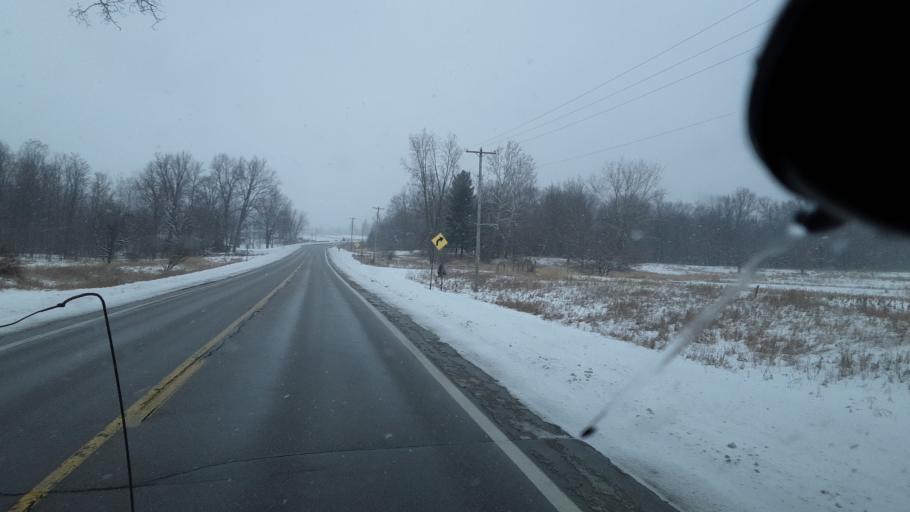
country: US
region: Michigan
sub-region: Jackson County
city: Jackson
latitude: 42.3091
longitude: -84.3883
